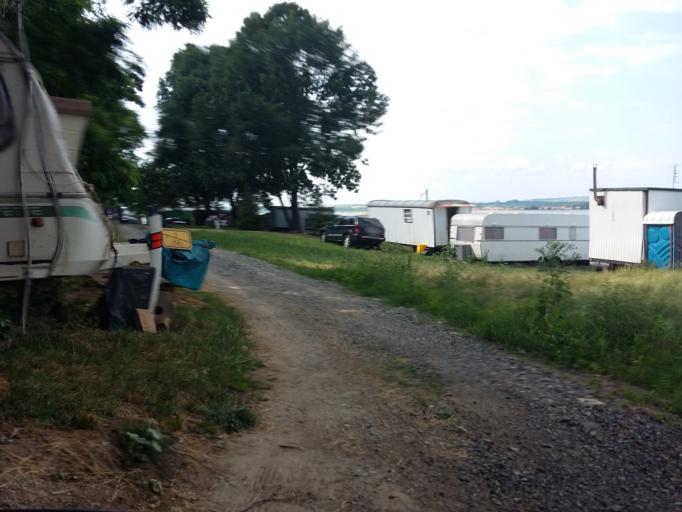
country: CZ
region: South Moravian
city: Sakvice
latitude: 48.8854
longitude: 16.6635
